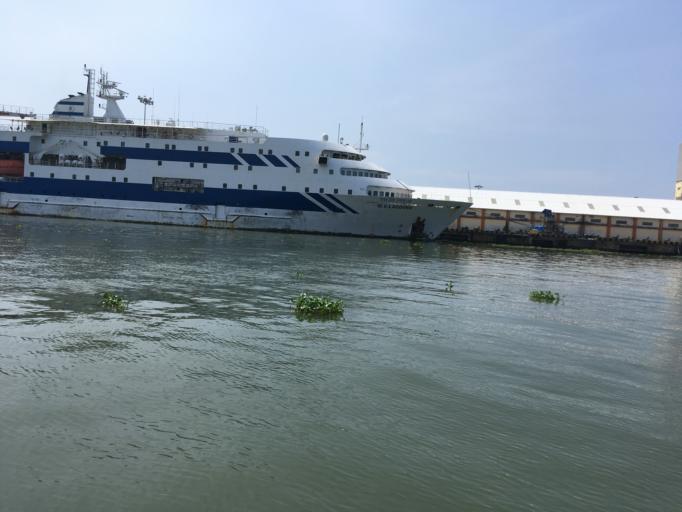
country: IN
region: Kerala
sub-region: Ernakulam
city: Cochin
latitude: 9.9698
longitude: 76.2651
